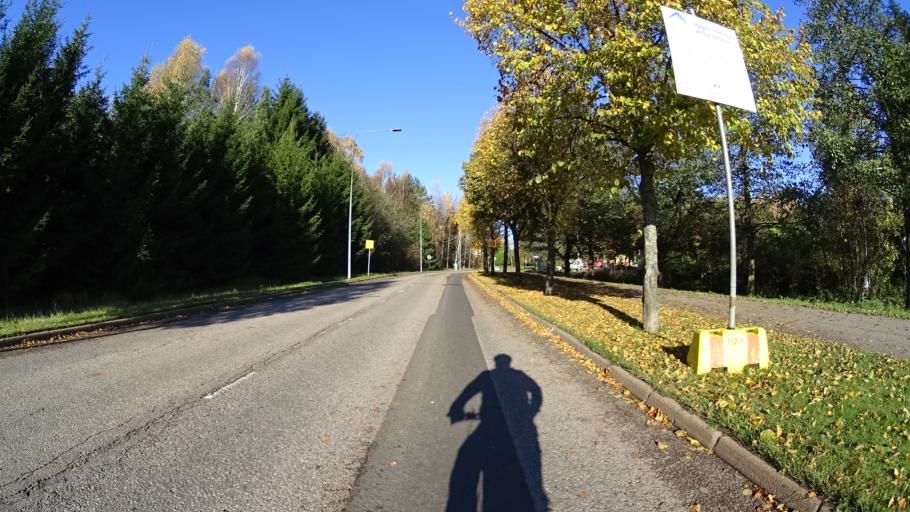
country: FI
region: Uusimaa
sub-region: Helsinki
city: Kilo
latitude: 60.2752
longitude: 24.7794
